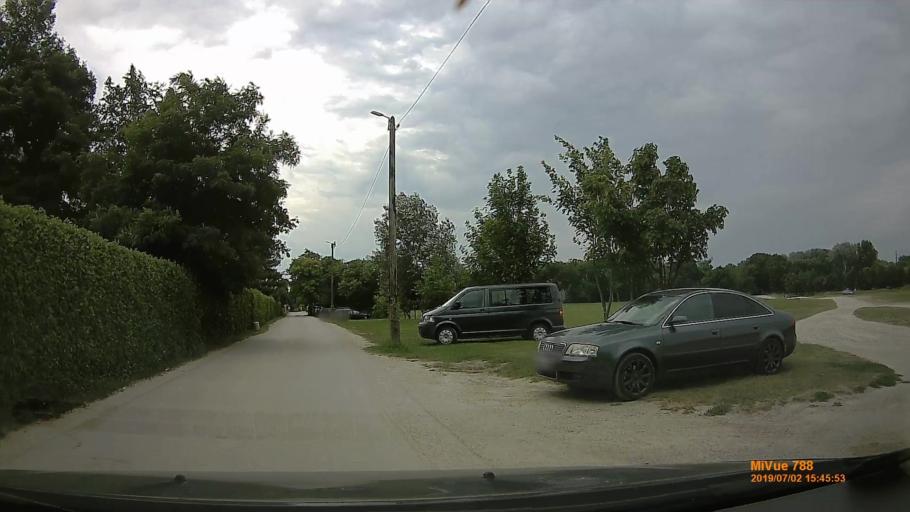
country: HU
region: Gyor-Moson-Sopron
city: Mosonmagyarovar
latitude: 47.8736
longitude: 17.2909
